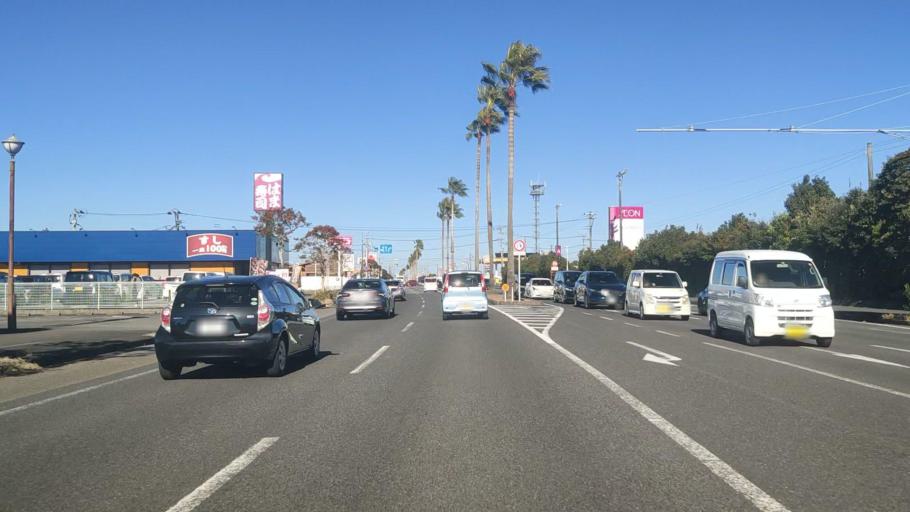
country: JP
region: Miyazaki
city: Miyazaki-shi
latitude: 31.9231
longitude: 131.4526
